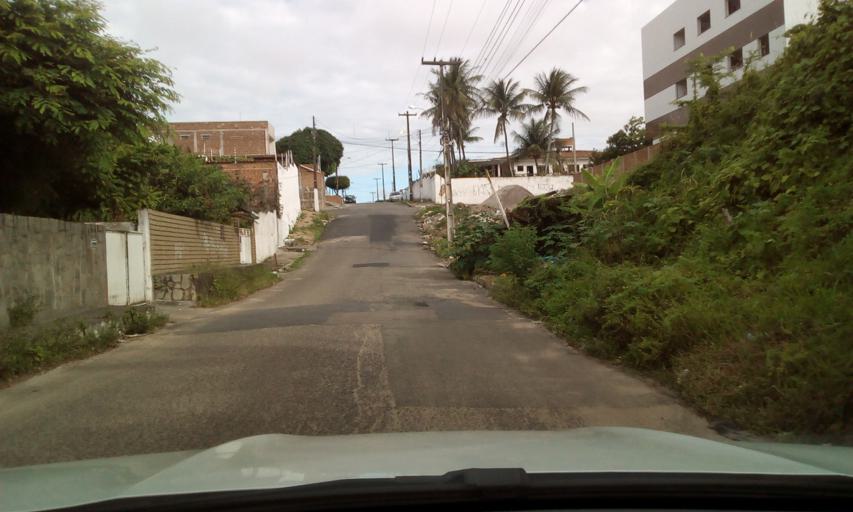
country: BR
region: Paraiba
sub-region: Joao Pessoa
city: Joao Pessoa
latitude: -7.1504
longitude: -34.8776
